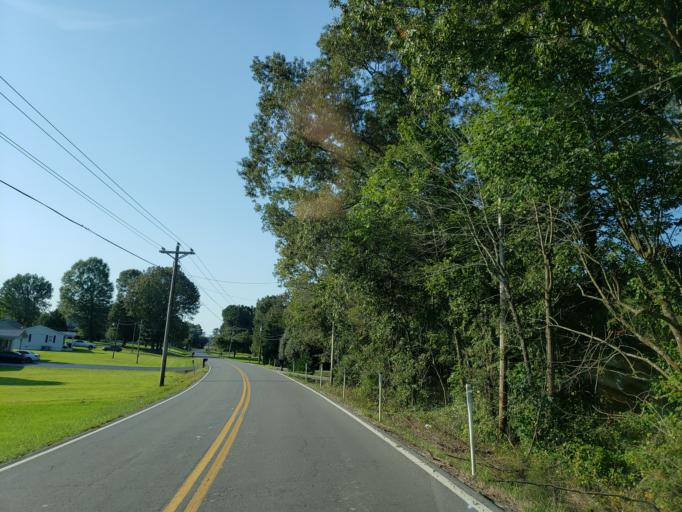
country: US
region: Tennessee
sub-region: Bradley County
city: Wildwood Lake
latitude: 35.0801
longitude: -84.7876
